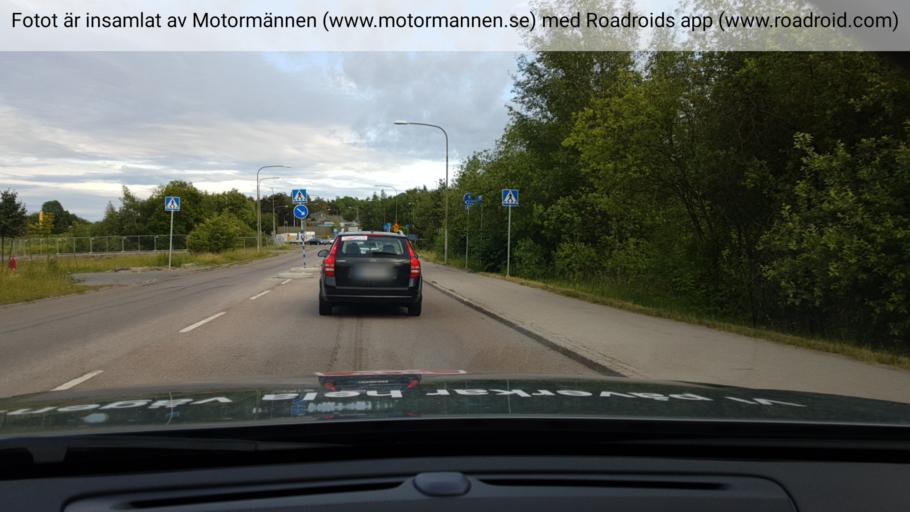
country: SE
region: Stockholm
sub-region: Stockholms Kommun
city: Arsta
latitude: 59.2875
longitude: 18.0427
